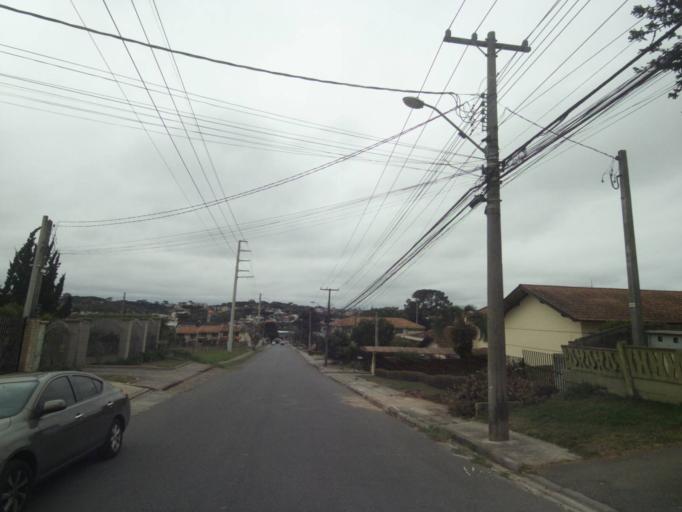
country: BR
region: Parana
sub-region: Sao Jose Dos Pinhais
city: Sao Jose dos Pinhais
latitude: -25.4845
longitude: -49.2266
